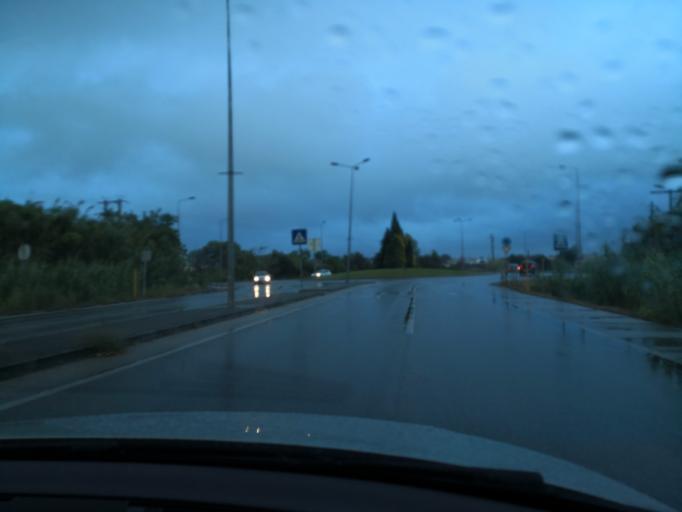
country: PT
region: Setubal
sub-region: Moita
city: Moita
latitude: 38.6506
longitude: -9.0003
